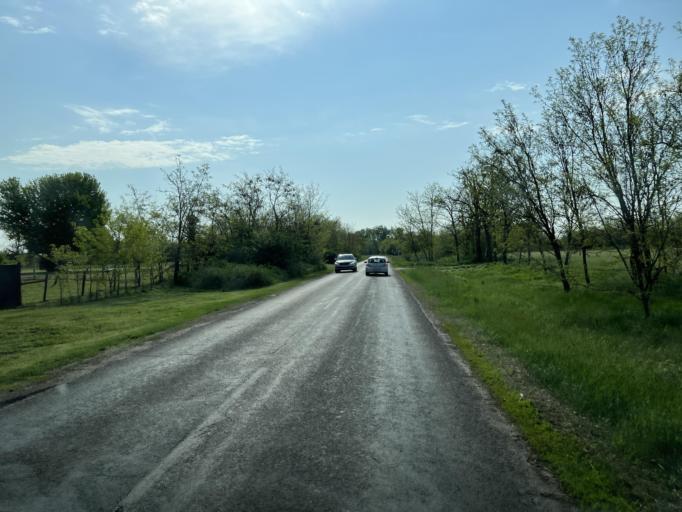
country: HU
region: Pest
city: Jaszkarajeno
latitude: 47.0403
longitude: 20.1060
